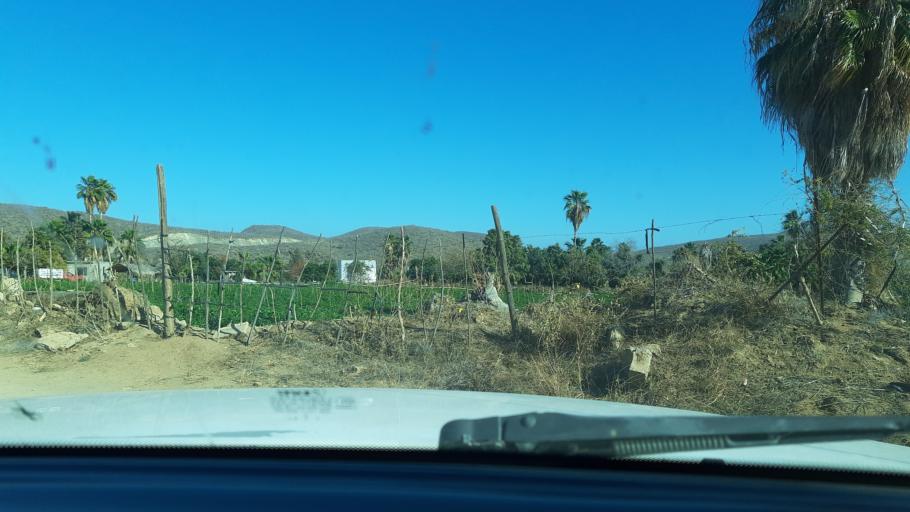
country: MX
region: Baja California Sur
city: Todos Santos
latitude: 23.4720
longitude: -110.2195
